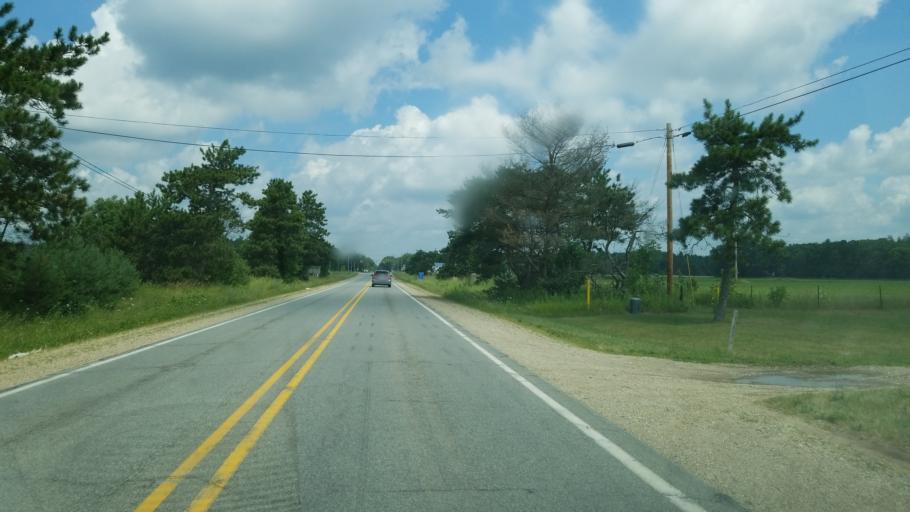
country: US
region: Michigan
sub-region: Montcalm County
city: Howard City
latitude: 43.4278
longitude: -85.4614
